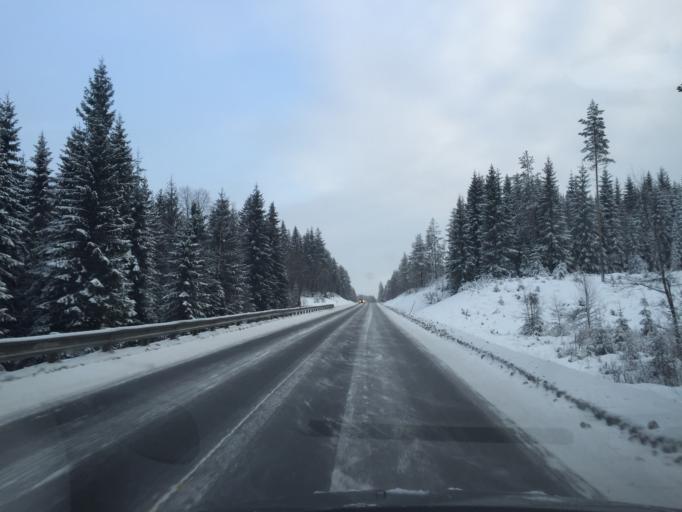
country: NO
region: Hedmark
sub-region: Elverum
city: Elverum
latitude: 60.9579
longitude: 11.7065
